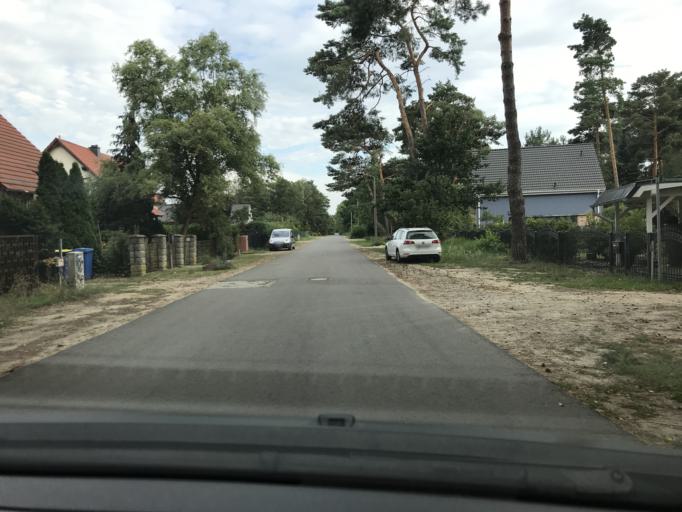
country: DE
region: Brandenburg
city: Wandlitz
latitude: 52.7111
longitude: 13.4463
